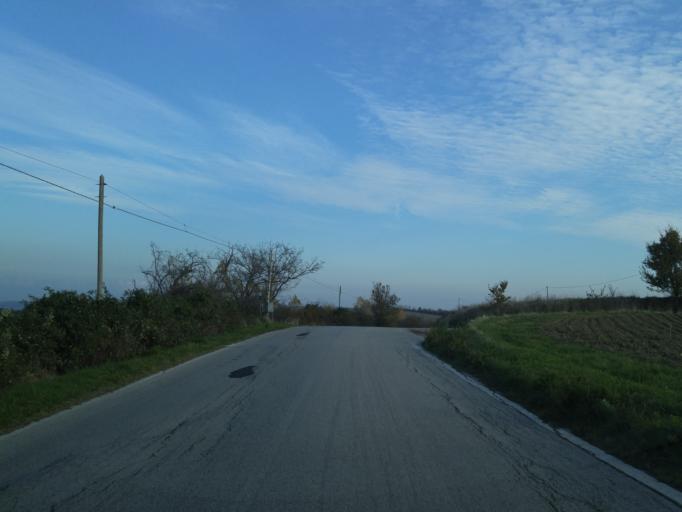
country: IT
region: The Marches
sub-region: Provincia di Pesaro e Urbino
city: Lucrezia
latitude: 43.7978
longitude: 12.9156
